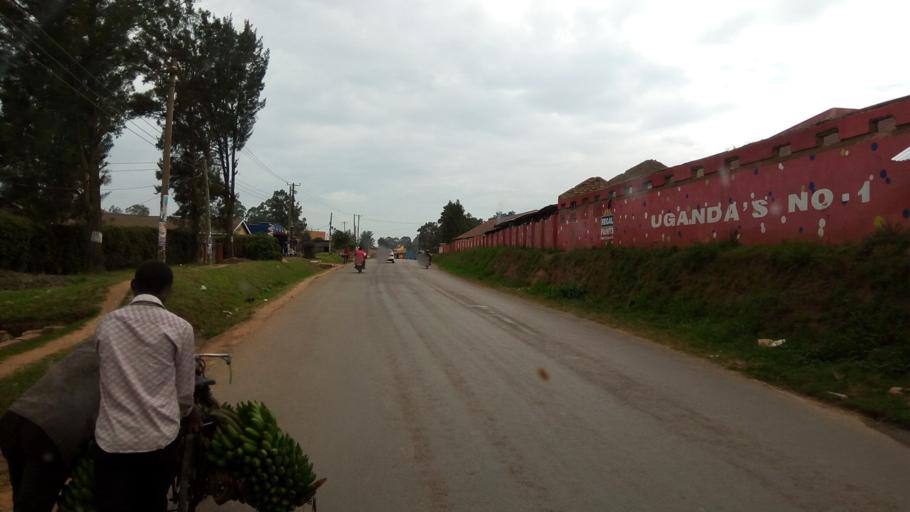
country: UG
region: Western Region
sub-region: Mbarara District
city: Mbarara
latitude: -0.6049
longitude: 30.6452
